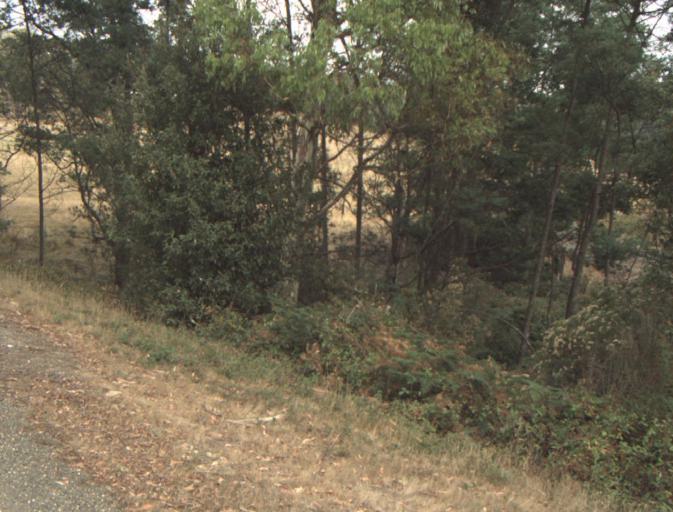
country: AU
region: Tasmania
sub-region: Dorset
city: Bridport
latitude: -41.1793
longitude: 147.2611
